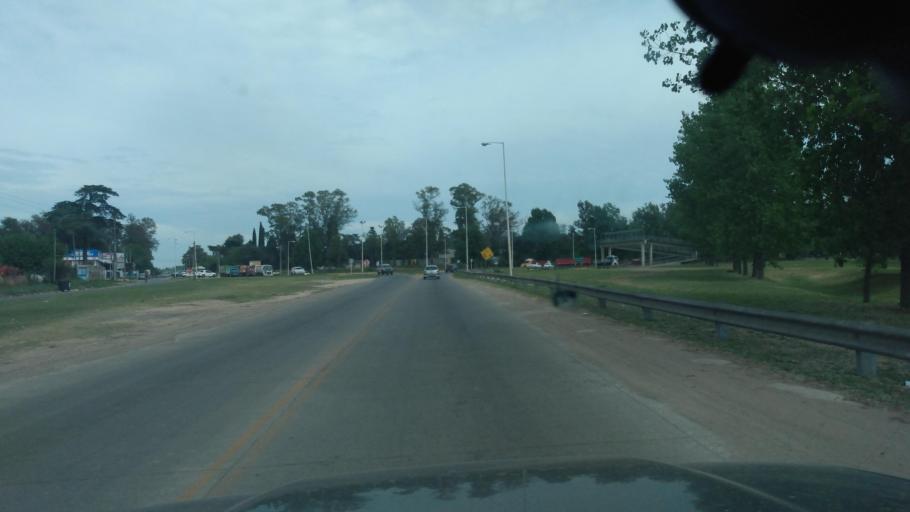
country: AR
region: Buenos Aires
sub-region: Partido de Lujan
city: Lujan
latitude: -34.5513
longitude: -59.1237
